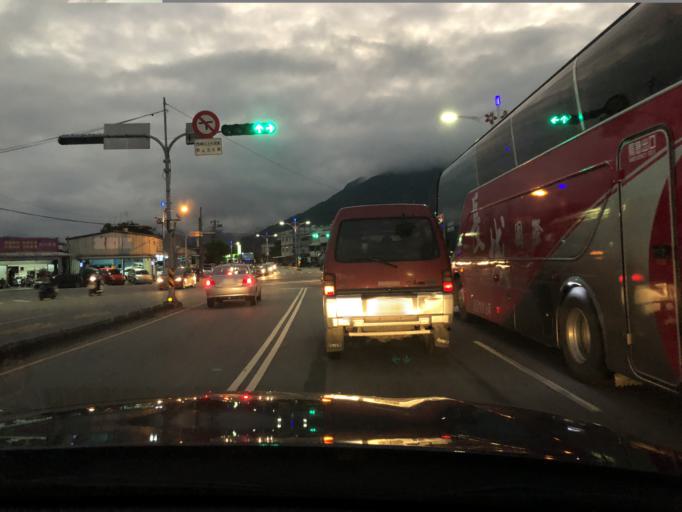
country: TW
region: Taiwan
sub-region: Hualien
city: Hualian
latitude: 23.9757
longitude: 121.5757
